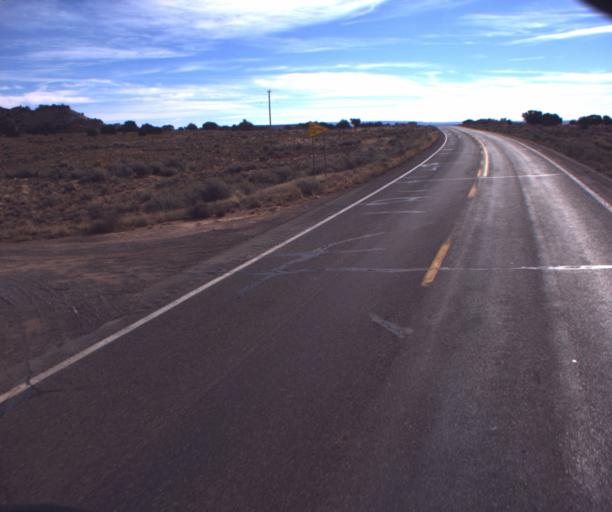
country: US
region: Arizona
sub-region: Coconino County
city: Kaibito
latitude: 36.6533
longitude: -111.2402
